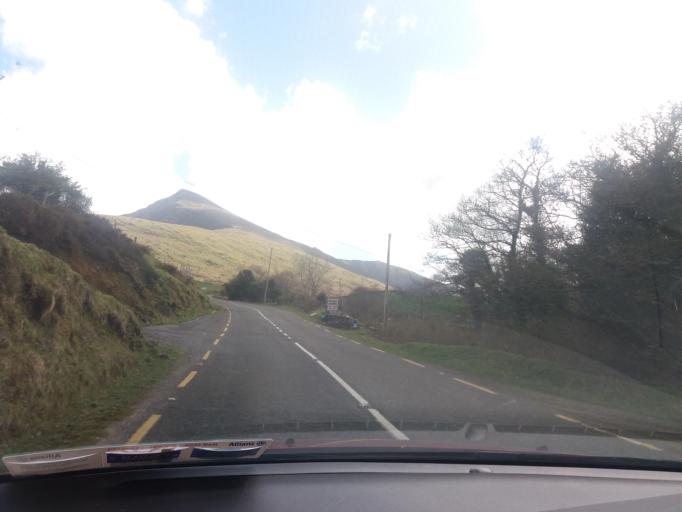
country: IE
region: Munster
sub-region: Ciarrai
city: Dingle
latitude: 52.2105
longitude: -10.1667
